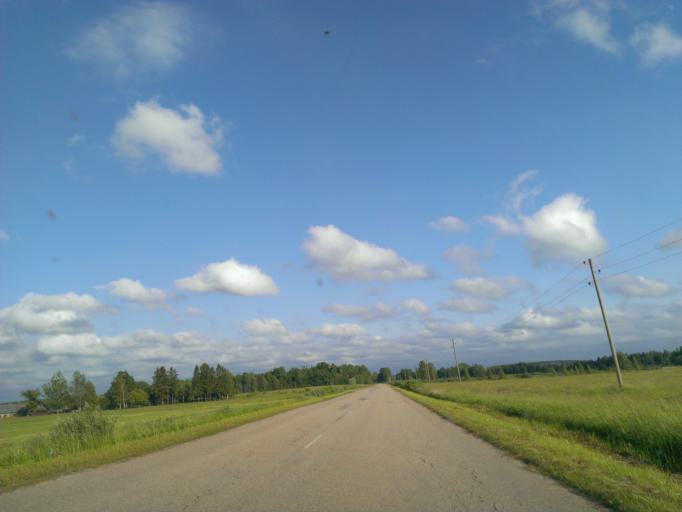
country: LV
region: Aizpute
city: Aizpute
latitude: 56.7966
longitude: 21.5009
